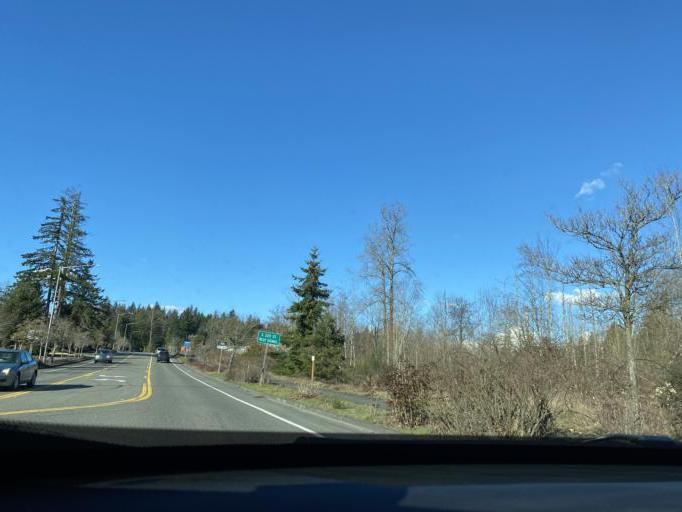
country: US
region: Washington
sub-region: King County
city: Lakeland North
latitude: 47.3119
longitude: -122.2889
